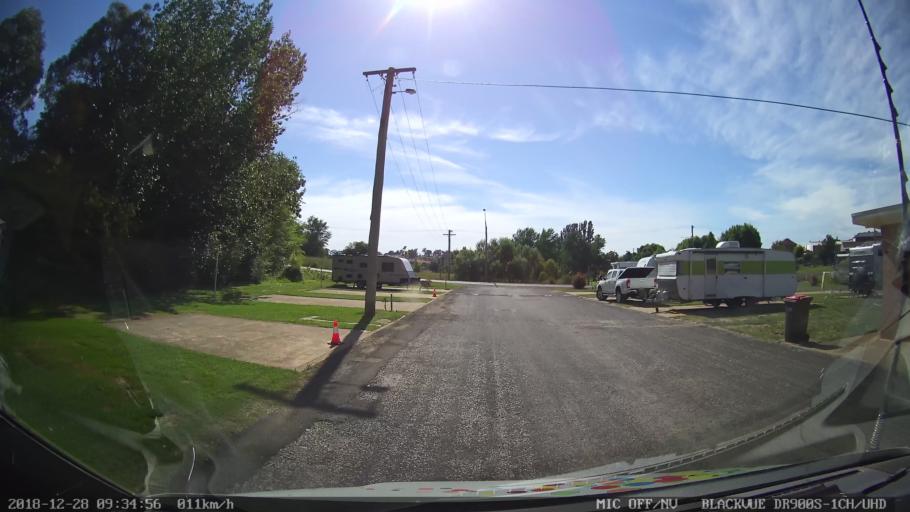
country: AU
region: New South Wales
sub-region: Upper Lachlan Shire
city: Crookwell
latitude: -34.4547
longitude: 149.4671
